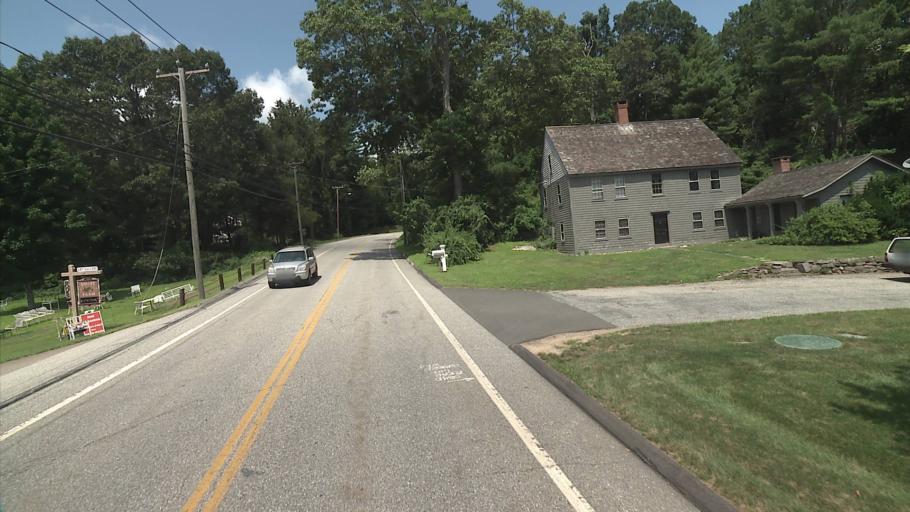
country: US
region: Connecticut
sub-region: Middlesex County
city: Essex Village
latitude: 41.3389
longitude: -72.3878
